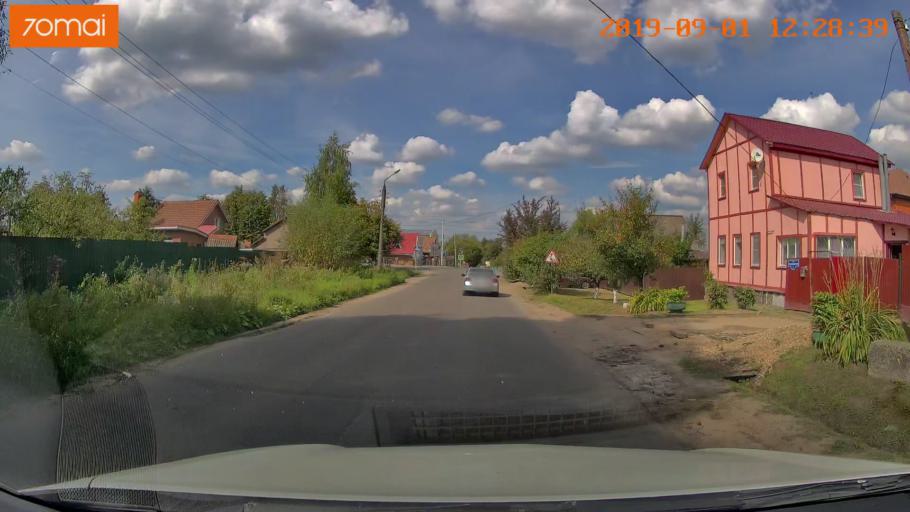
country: RU
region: Kaluga
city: Maloyaroslavets
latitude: 55.0072
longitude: 36.4516
